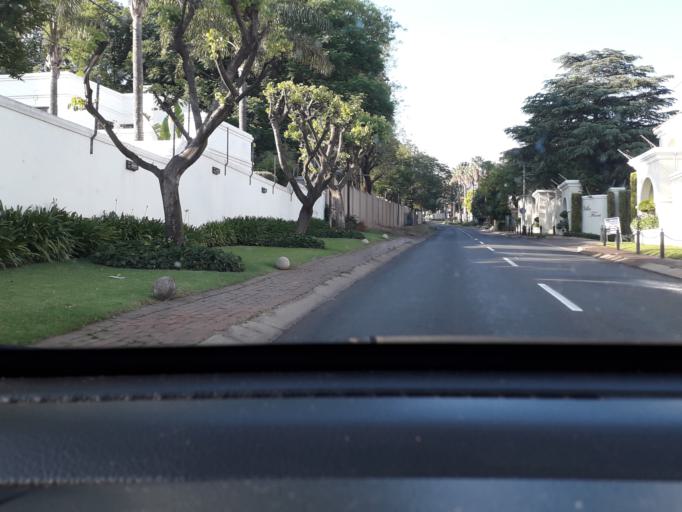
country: ZA
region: Gauteng
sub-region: City of Johannesburg Metropolitan Municipality
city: Modderfontein
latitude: -26.0865
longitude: 28.0561
